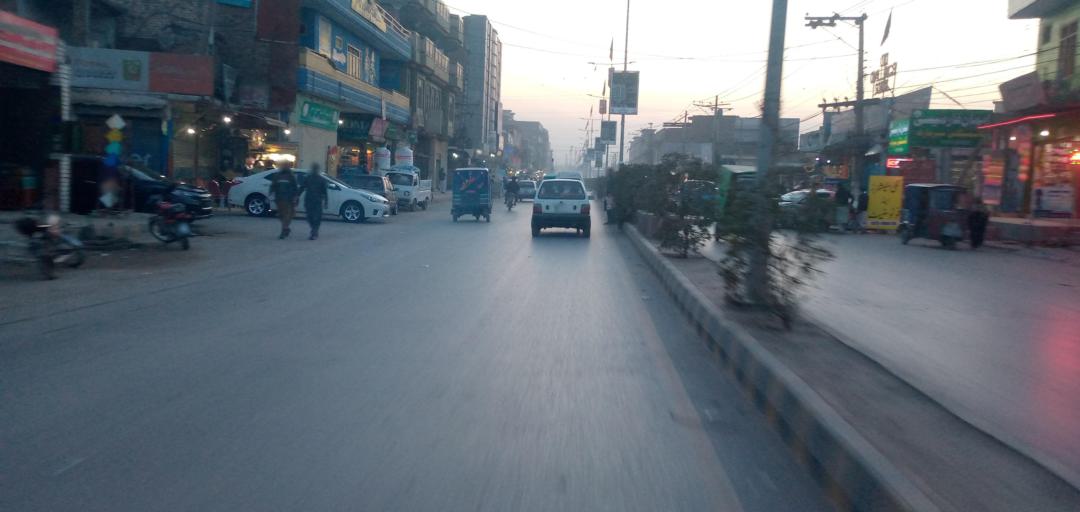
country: PK
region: Khyber Pakhtunkhwa
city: Peshawar
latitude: 34.0304
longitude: 71.6037
